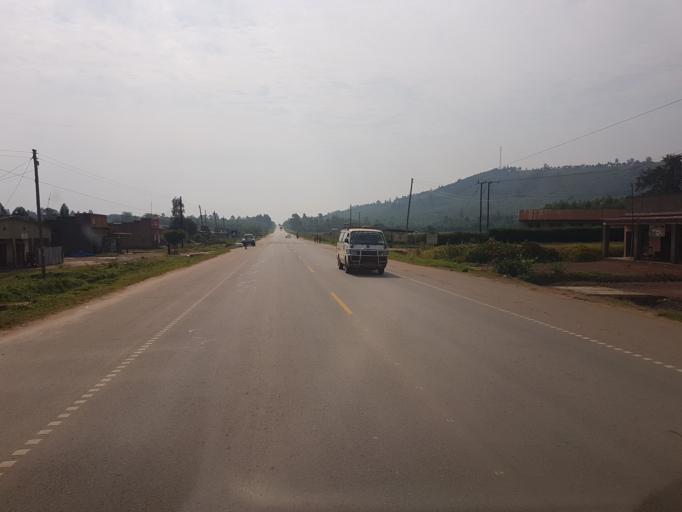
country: UG
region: Western Region
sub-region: Sheema District
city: Kibingo
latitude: -0.6418
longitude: 30.5038
